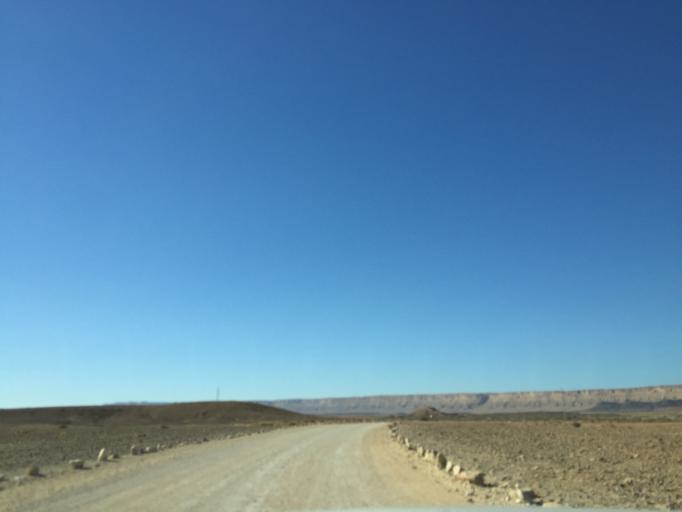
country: IL
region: Southern District
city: Mitzpe Ramon
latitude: 30.6244
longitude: 34.9233
